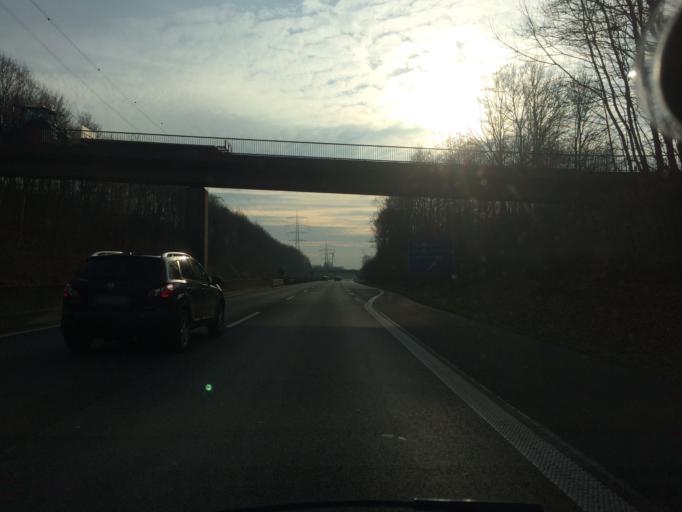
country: DE
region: North Rhine-Westphalia
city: Dorsten
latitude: 51.6119
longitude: 6.9394
